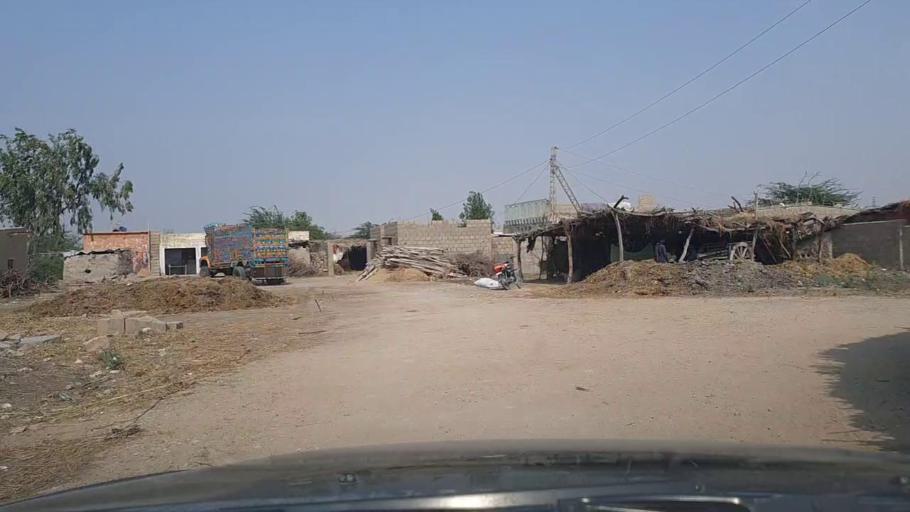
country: PK
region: Sindh
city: Thatta
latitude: 24.8042
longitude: 67.9084
